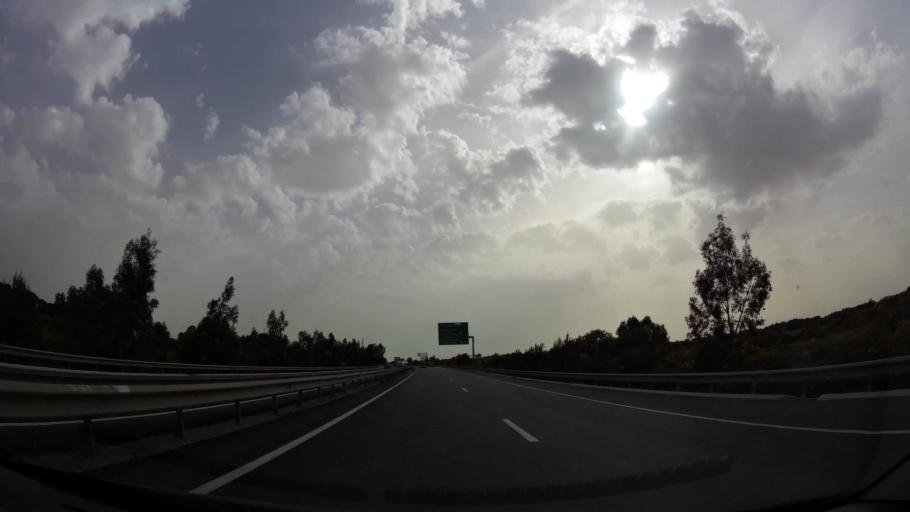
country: MA
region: Tanger-Tetouan
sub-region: Tanger-Assilah
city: Boukhalef
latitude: 35.6734
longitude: -5.9348
